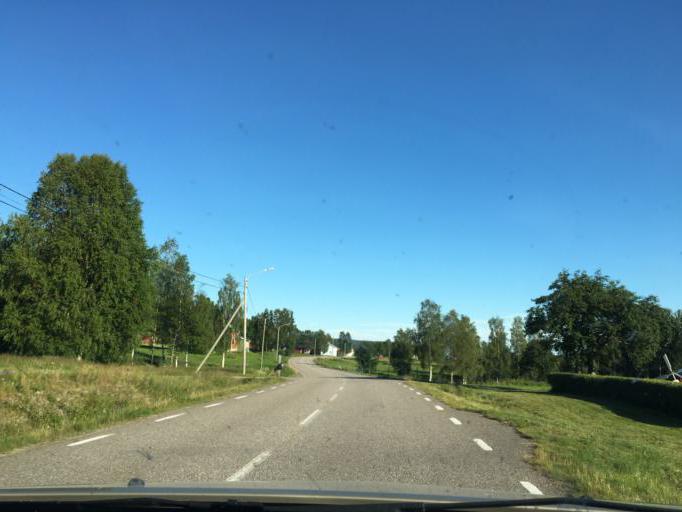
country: SE
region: Norrbotten
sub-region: Kalix Kommun
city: Rolfs
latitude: 65.9019
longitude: 22.9320
